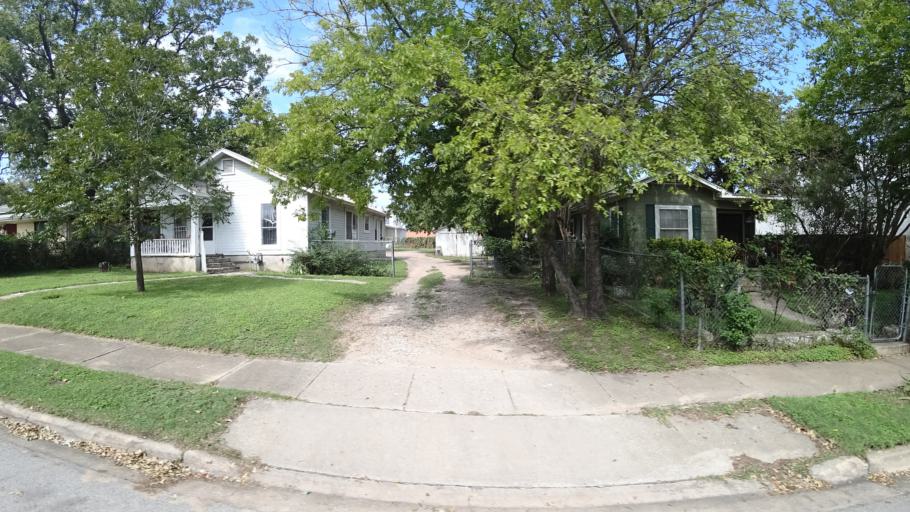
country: US
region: Texas
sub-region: Travis County
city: Austin
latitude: 30.2727
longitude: -97.7202
